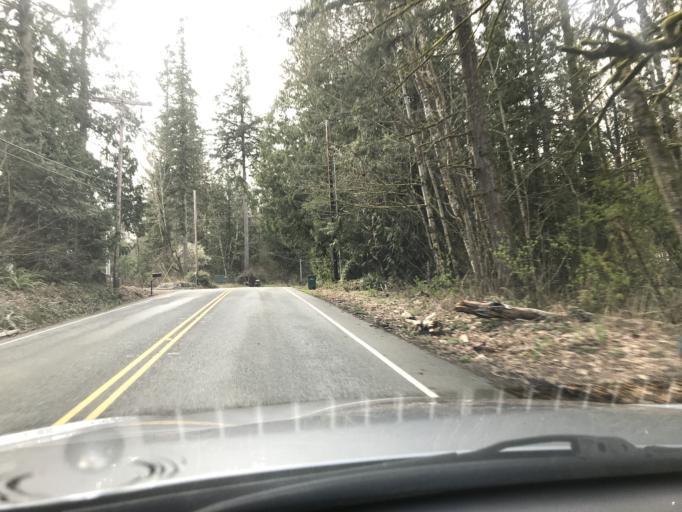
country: US
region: Washington
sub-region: King County
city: Ames Lake
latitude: 47.6491
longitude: -121.9714
